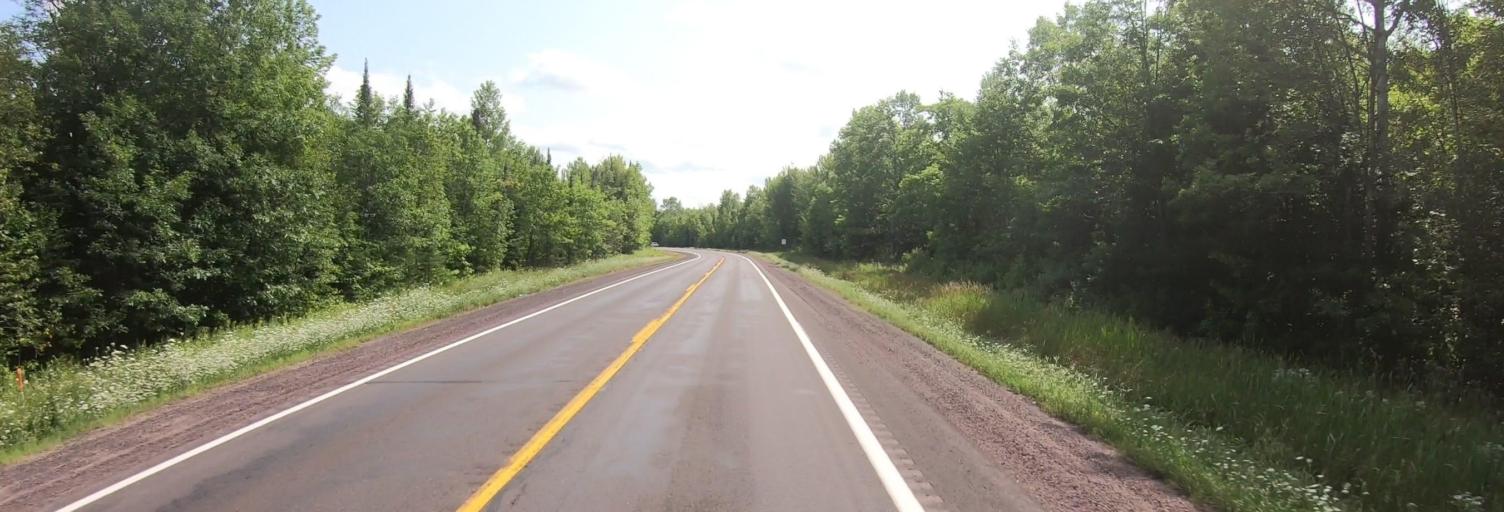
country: US
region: Michigan
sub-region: Ontonagon County
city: Ontonagon
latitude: 46.8296
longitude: -88.9967
